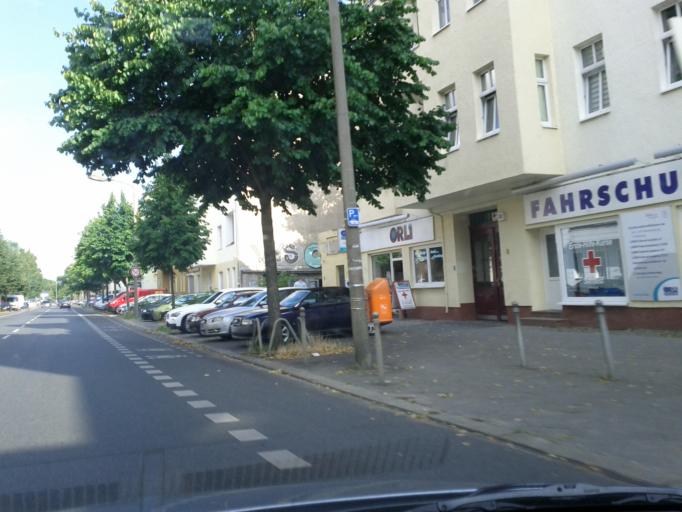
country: DE
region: Berlin
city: Oberschoneweide
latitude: 52.4530
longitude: 13.5245
